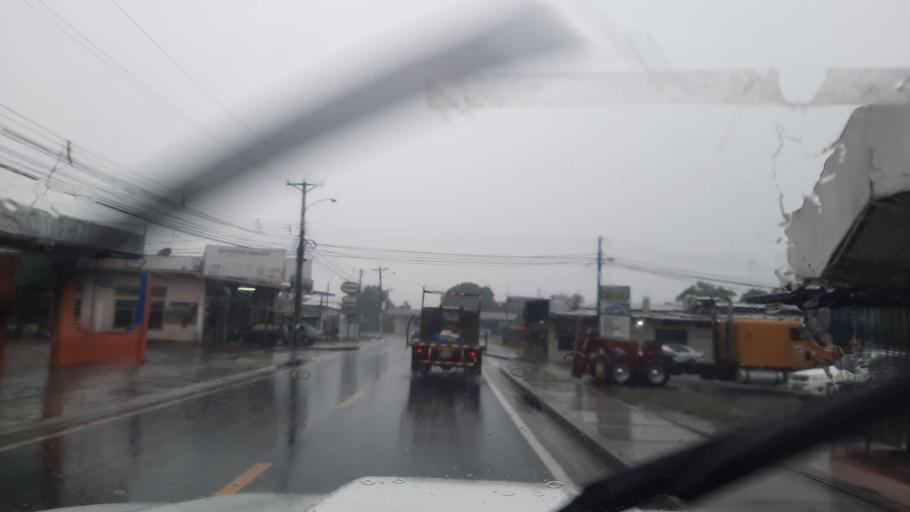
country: PA
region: Chiriqui
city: La Concepcion
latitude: 8.5155
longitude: -82.6225
